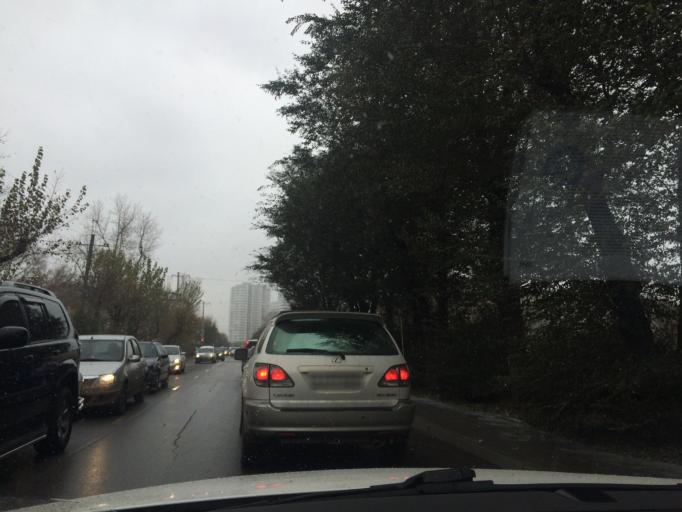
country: KZ
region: Astana Qalasy
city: Astana
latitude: 51.1684
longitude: 71.4492
